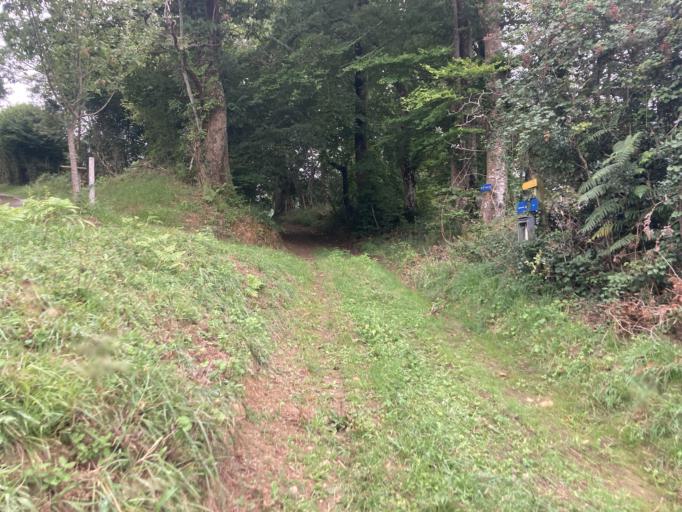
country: FR
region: Aquitaine
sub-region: Departement des Pyrenees-Atlantiques
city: Ledeuix
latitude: 43.2292
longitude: -0.5609
